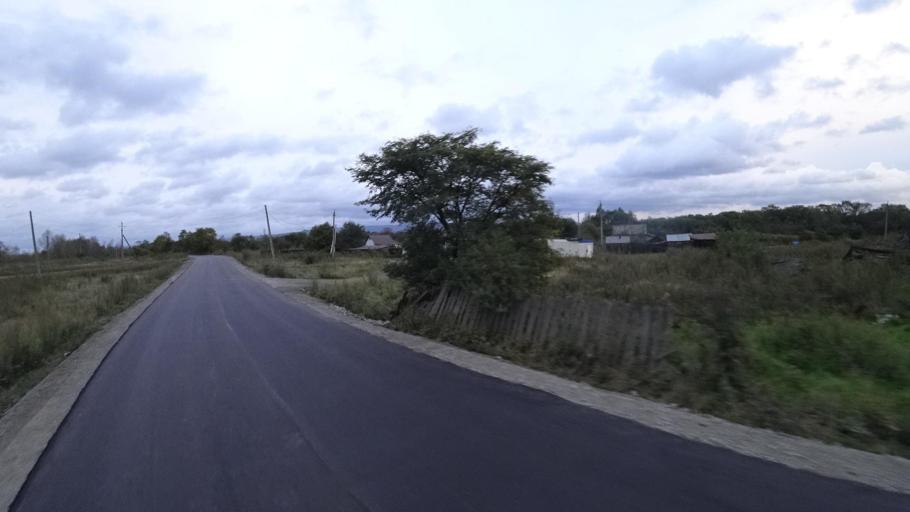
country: RU
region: Jewish Autonomous Oblast
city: Izvestkovyy
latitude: 48.9906
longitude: 131.5459
